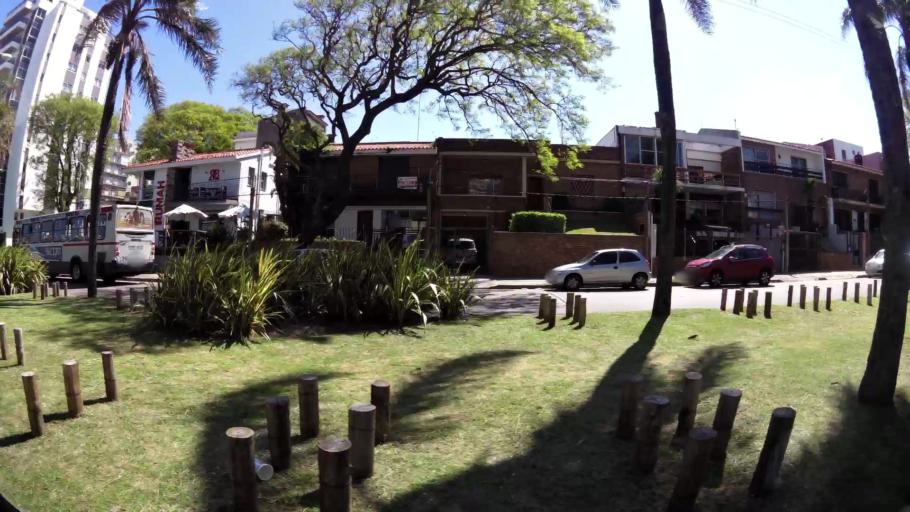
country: UY
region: Montevideo
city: Montevideo
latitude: -34.9084
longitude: -56.1359
